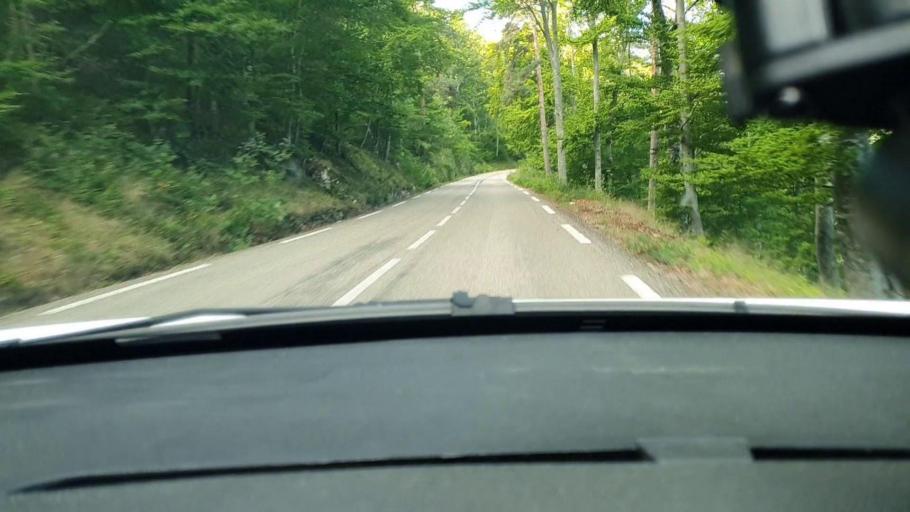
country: FR
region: Rhone-Alpes
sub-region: Departement de l'Ardeche
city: Les Vans
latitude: 44.4295
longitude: 4.0146
